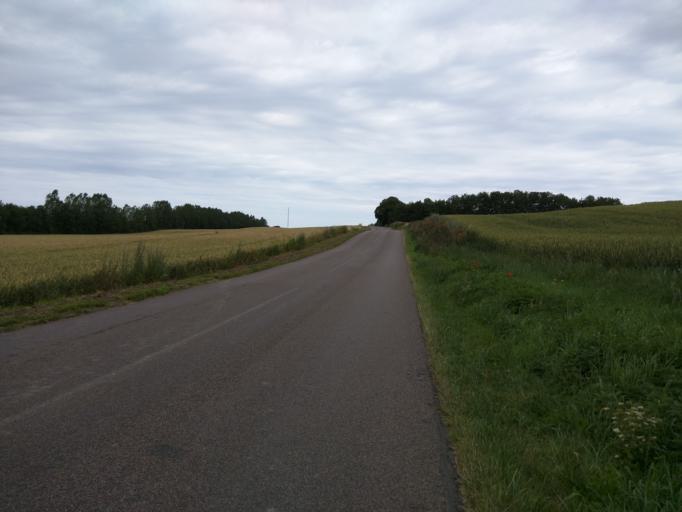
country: DK
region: Zealand
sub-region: Kalundborg Kommune
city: Svebolle
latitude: 55.6987
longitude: 11.3061
